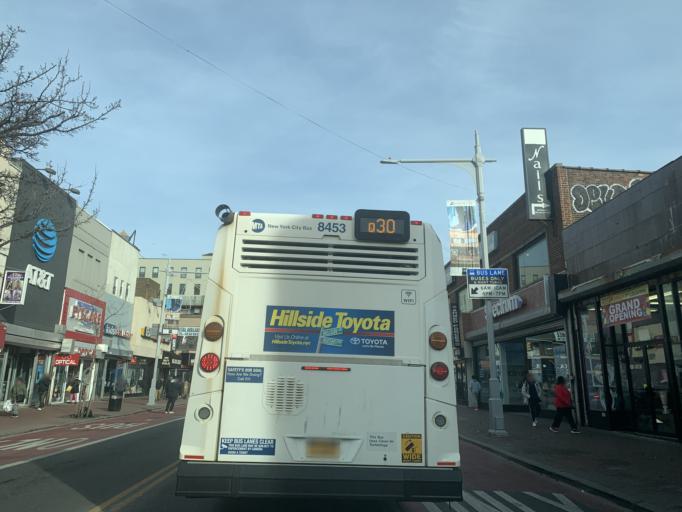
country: US
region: New York
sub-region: Queens County
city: Jamaica
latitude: 40.7052
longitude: -73.7956
